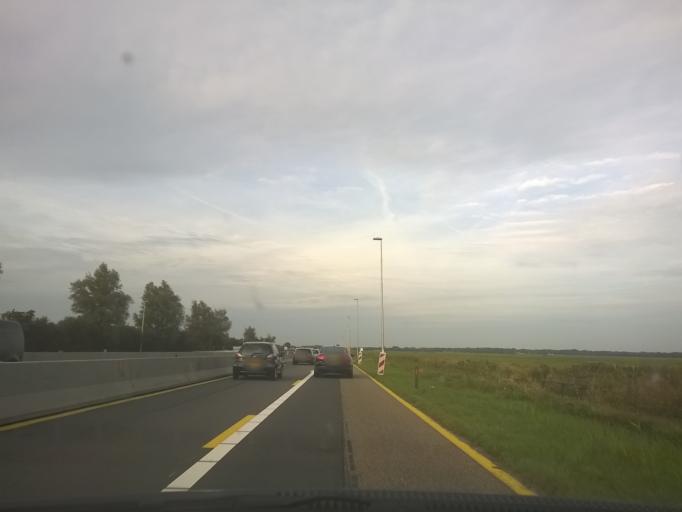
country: NL
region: Friesland
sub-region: Gemeente Smallingerland
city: Boornbergum
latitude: 53.0452
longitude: 6.0355
